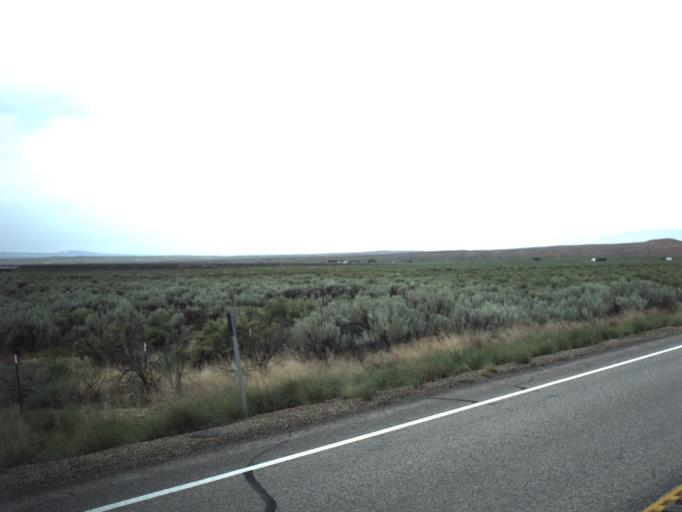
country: US
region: Utah
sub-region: Carbon County
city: East Carbon City
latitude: 39.5307
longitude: -110.5589
